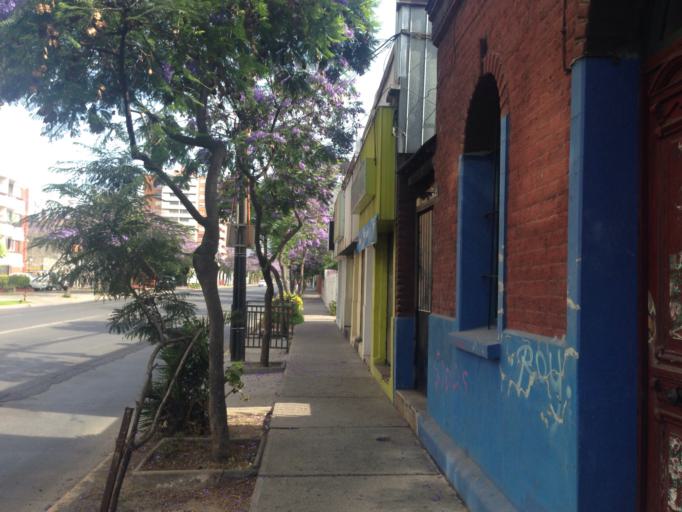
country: CL
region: Santiago Metropolitan
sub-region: Provincia de Santiago
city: Santiago
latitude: -33.4525
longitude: -70.6208
